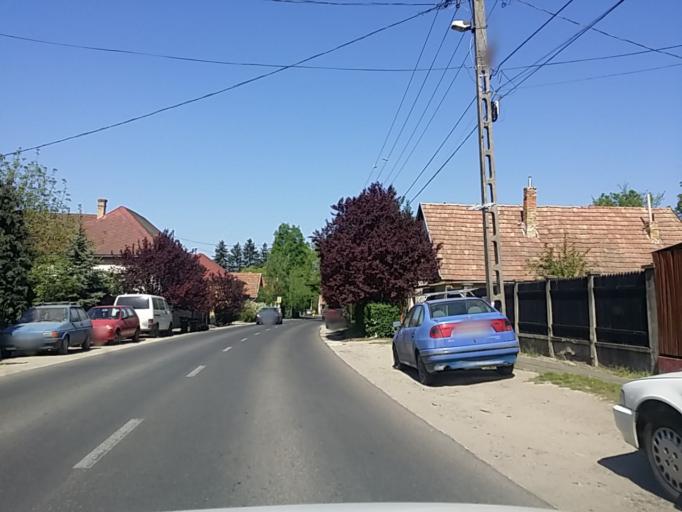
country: HU
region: Pest
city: Fot
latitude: 47.6044
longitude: 19.2048
